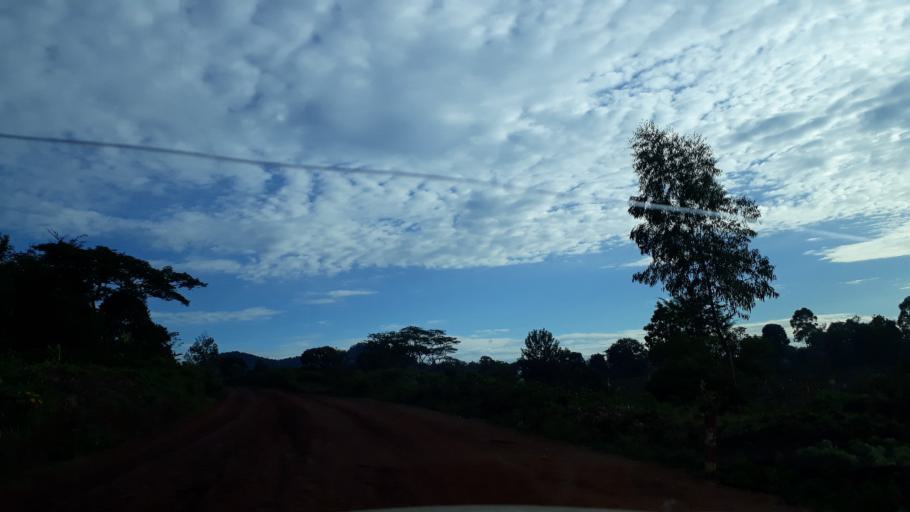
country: UG
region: Northern Region
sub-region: Zombo District
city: Paidha
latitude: 2.2440
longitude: 30.8620
